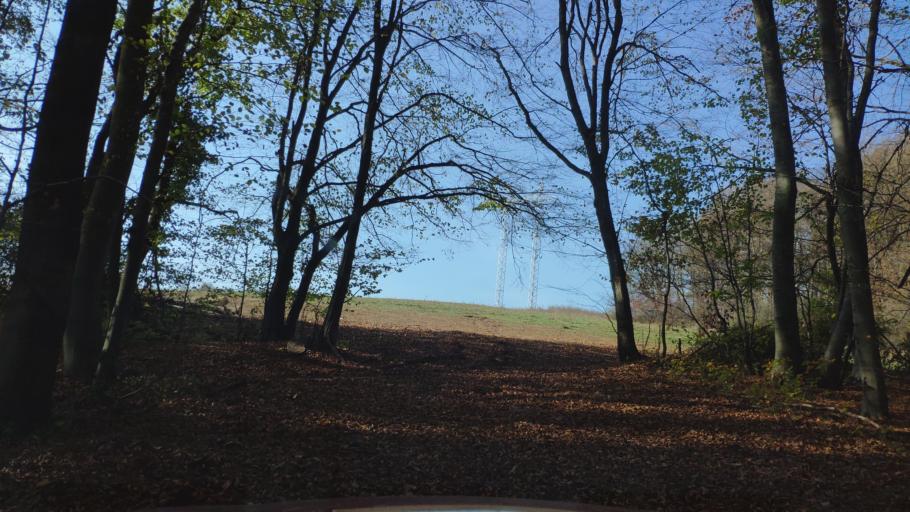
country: SK
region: Presovsky
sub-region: Okres Presov
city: Presov
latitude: 48.8956
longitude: 21.2271
